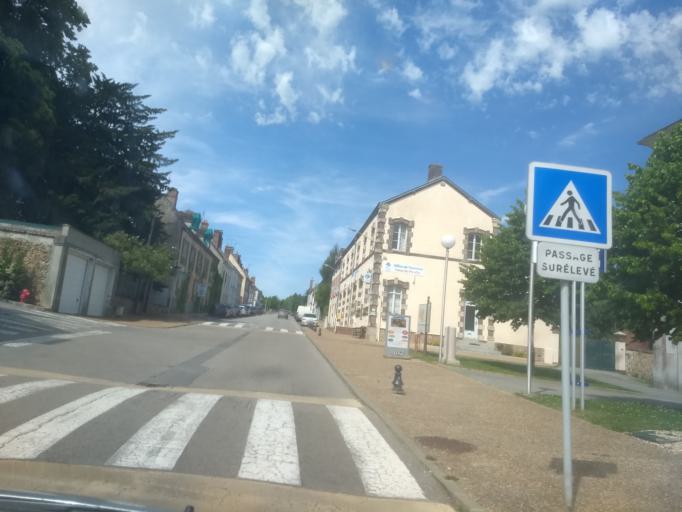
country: FR
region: Lower Normandy
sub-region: Departement de l'Orne
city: Remalard
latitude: 48.4301
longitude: 0.7739
